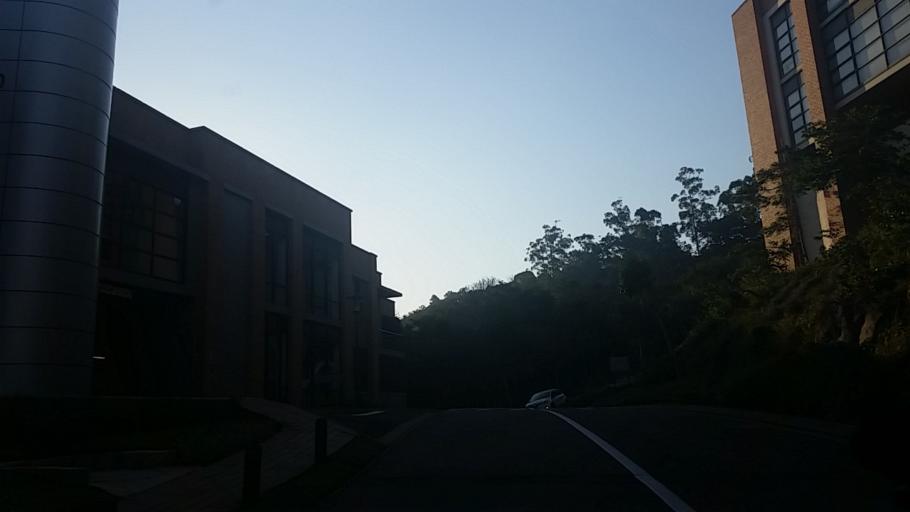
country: ZA
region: KwaZulu-Natal
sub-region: eThekwini Metropolitan Municipality
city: Berea
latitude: -29.8473
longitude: 30.9255
